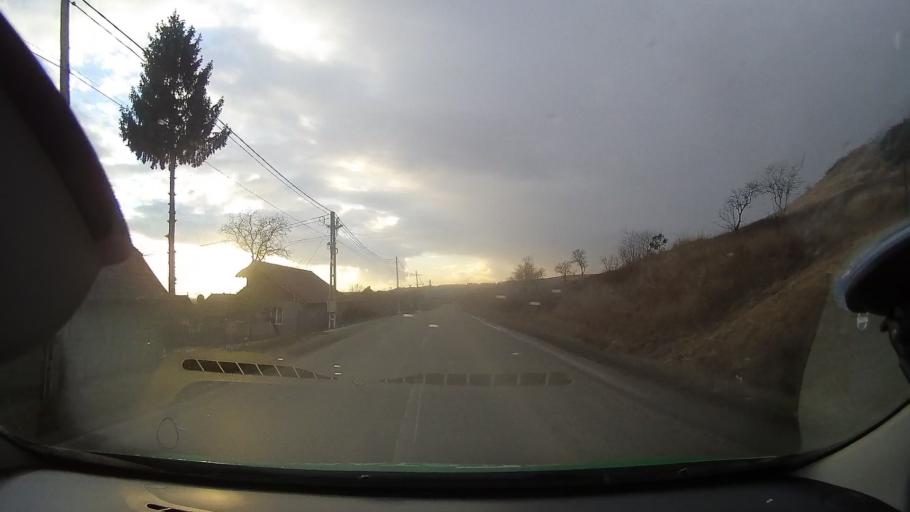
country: RO
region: Alba
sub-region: Comuna Lunca Muresului
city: Lunca Muresului
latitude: 46.4285
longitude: 23.8971
